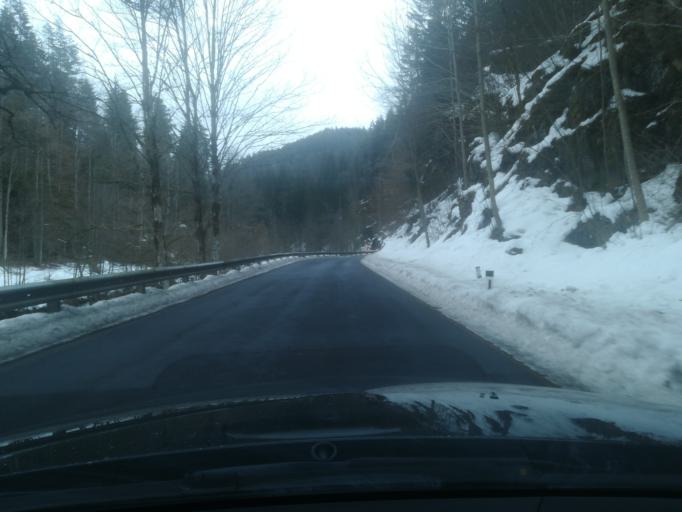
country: AT
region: Upper Austria
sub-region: Politischer Bezirk Perg
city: Perg
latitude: 48.4101
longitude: 14.6355
